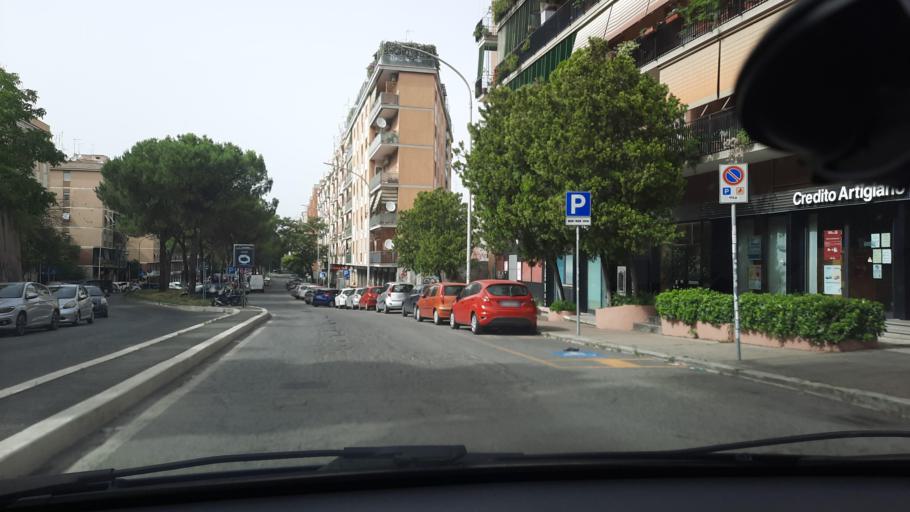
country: IT
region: Latium
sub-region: Citta metropolitana di Roma Capitale
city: Rome
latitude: 41.8538
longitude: 12.4805
